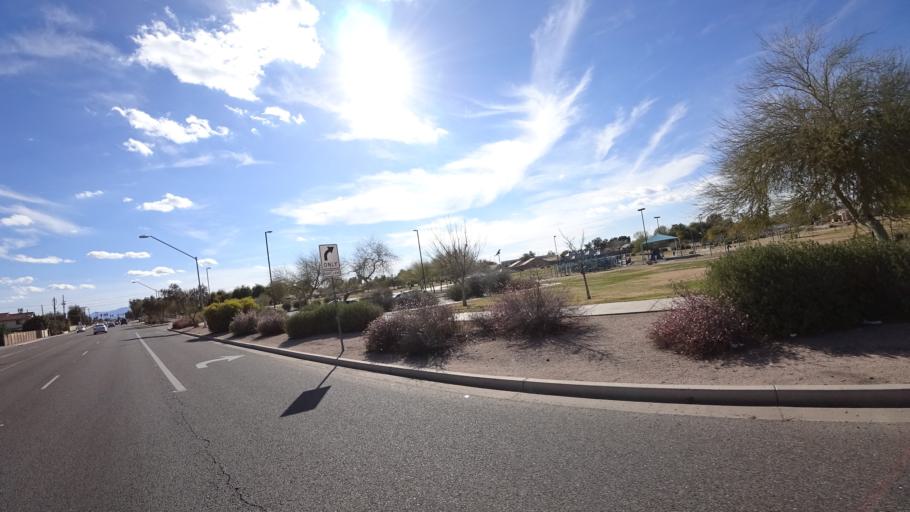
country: US
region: Arizona
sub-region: Maricopa County
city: Glendale
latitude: 33.5119
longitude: -112.2205
